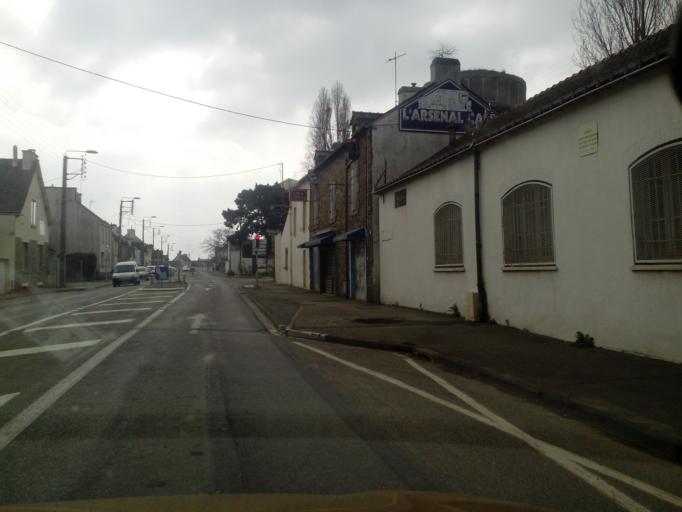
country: FR
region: Brittany
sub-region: Departement du Morbihan
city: Vannes
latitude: 47.6653
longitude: -2.7371
